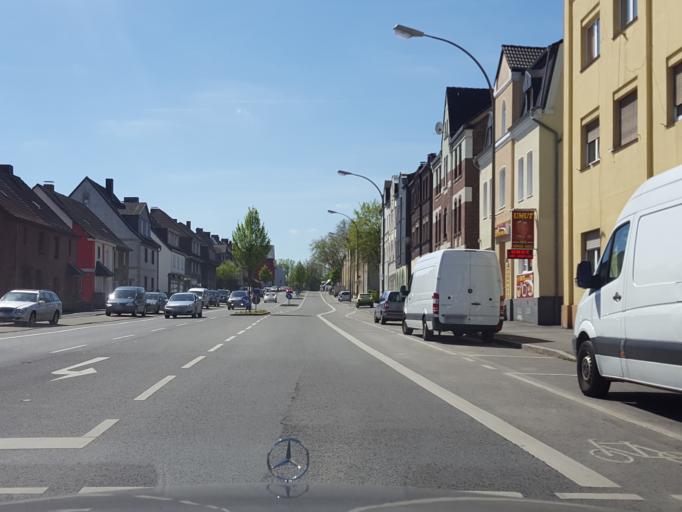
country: DE
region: North Rhine-Westphalia
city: Castrop-Rauxel
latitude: 51.5180
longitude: 7.3244
